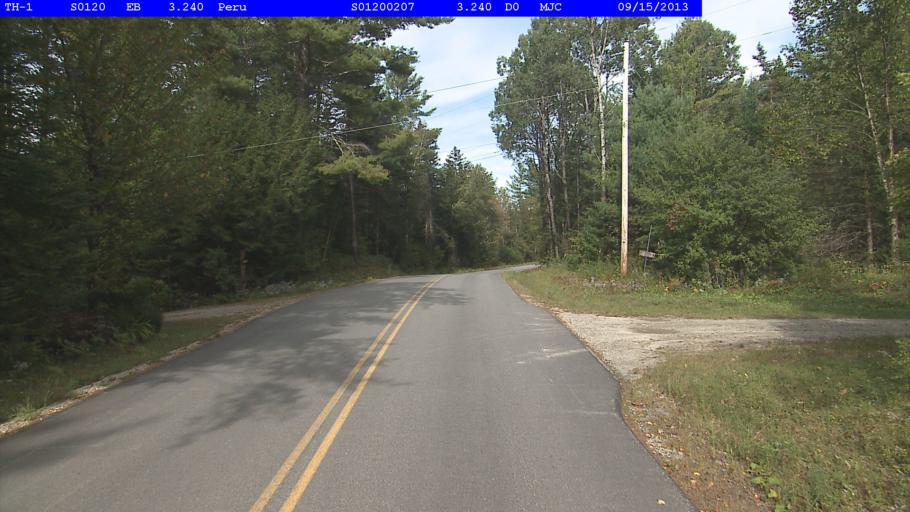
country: US
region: Vermont
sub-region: Bennington County
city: Manchester Center
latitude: 43.2627
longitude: -72.8692
